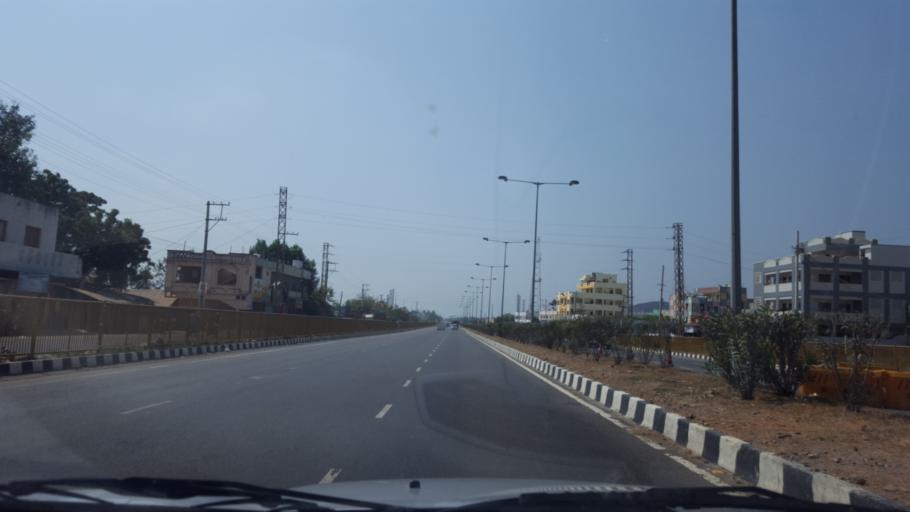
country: IN
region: Andhra Pradesh
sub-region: Guntur
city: Chilakalurupet
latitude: 15.9808
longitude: 80.1012
